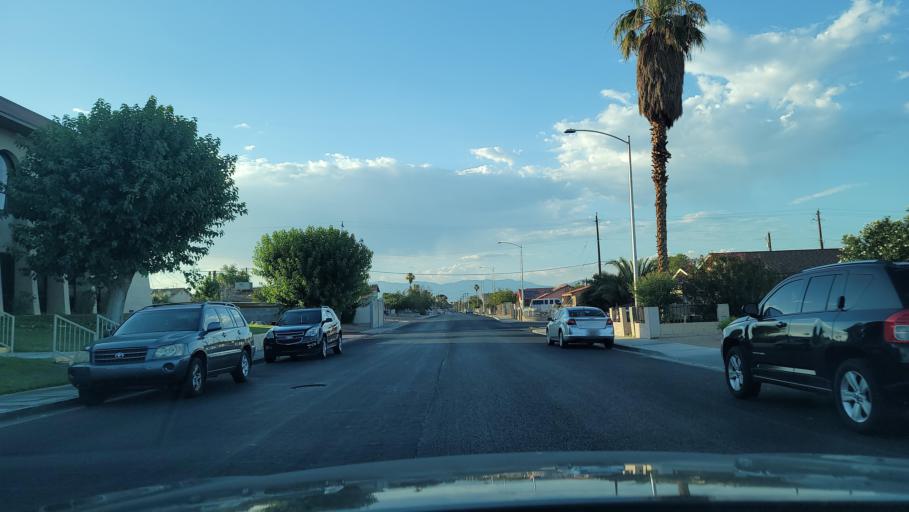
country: US
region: Nevada
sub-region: Clark County
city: Winchester
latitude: 36.1456
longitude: -115.1232
